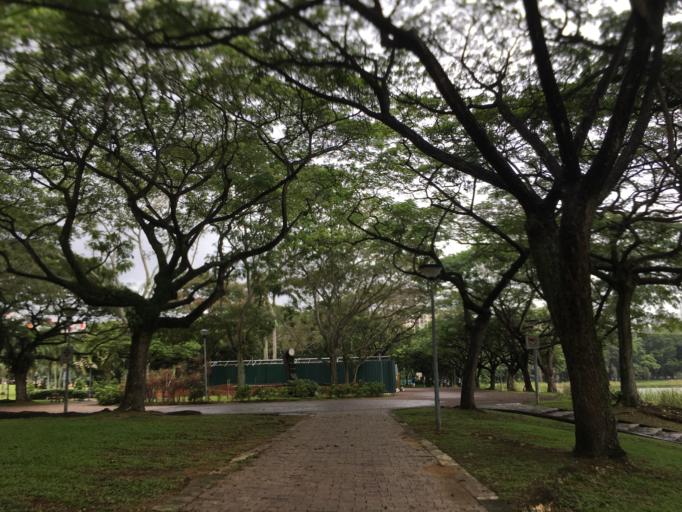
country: SG
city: Singapore
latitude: 1.3758
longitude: 103.8979
